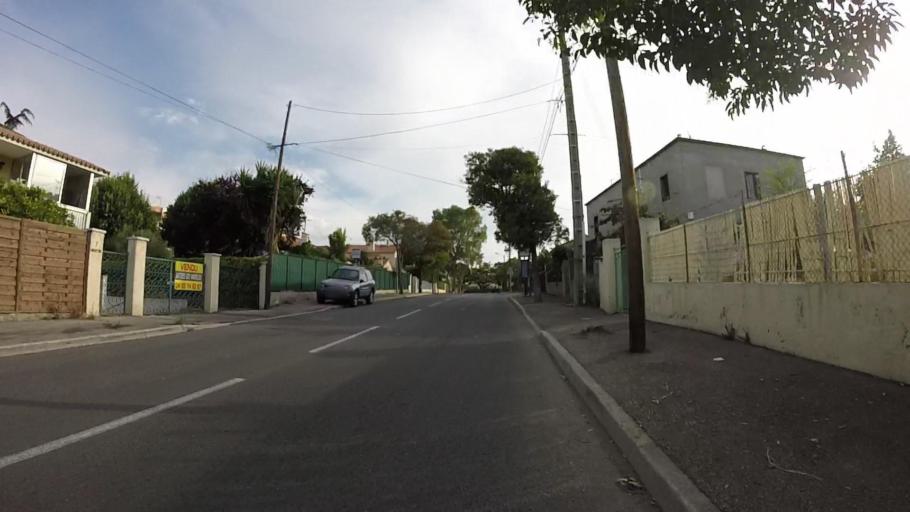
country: FR
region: Provence-Alpes-Cote d'Azur
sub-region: Departement des Alpes-Maritimes
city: Antibes
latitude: 43.5844
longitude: 7.1069
